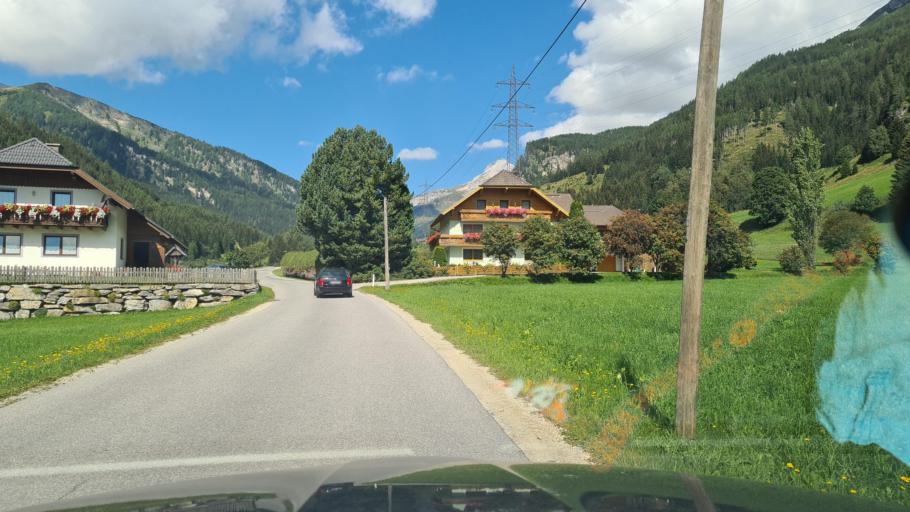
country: AT
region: Salzburg
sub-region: Politischer Bezirk Tamsweg
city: Zederhaus
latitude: 47.1662
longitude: 13.4726
